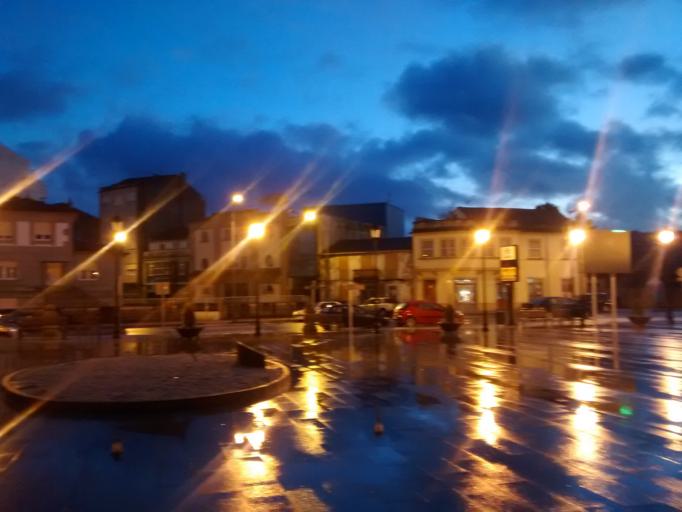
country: ES
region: Galicia
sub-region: Provincia de Pontevedra
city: A Estrada
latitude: 42.6886
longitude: -8.4892
